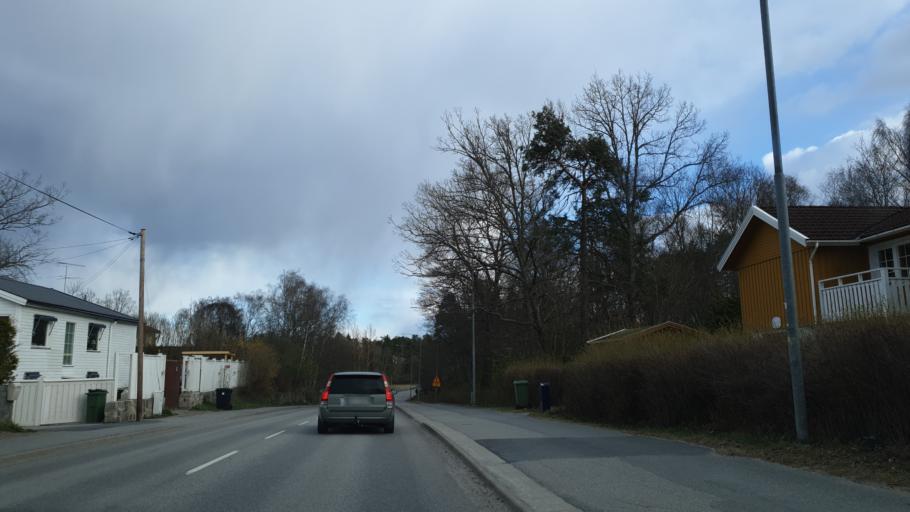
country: SE
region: Stockholm
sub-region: Lidingo
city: Lidingoe
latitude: 59.3746
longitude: 18.1309
